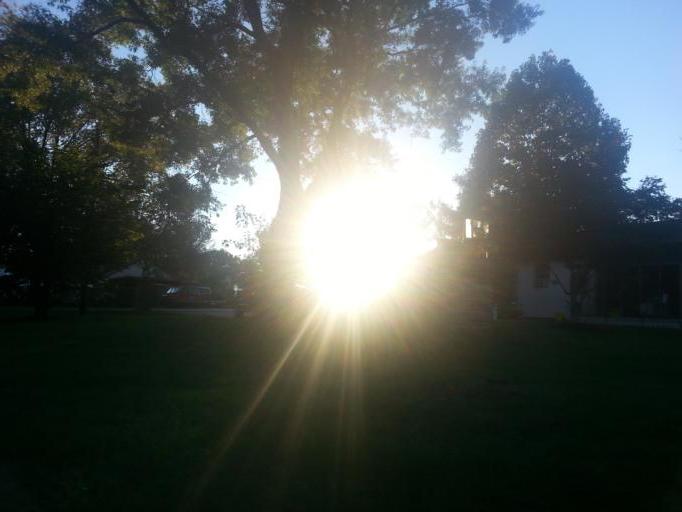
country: US
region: Tennessee
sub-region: Blount County
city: Alcoa
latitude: 35.7821
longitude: -83.9567
